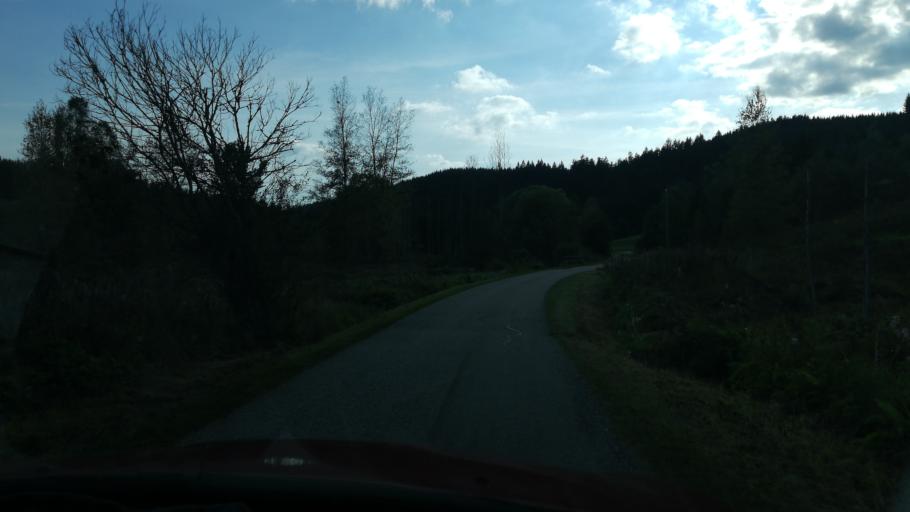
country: AT
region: Lower Austria
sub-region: Politischer Bezirk Zwettl
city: Langschlag
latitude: 48.4914
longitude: 14.8426
